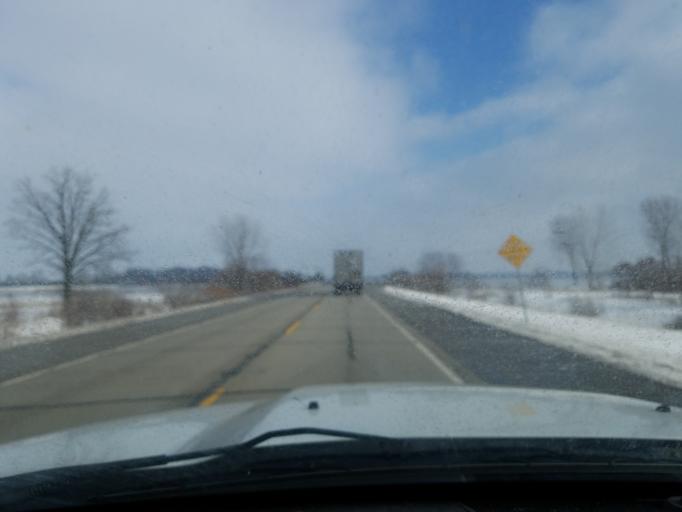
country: US
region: Indiana
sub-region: Marshall County
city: Bremen
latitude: 41.4606
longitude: -86.1803
